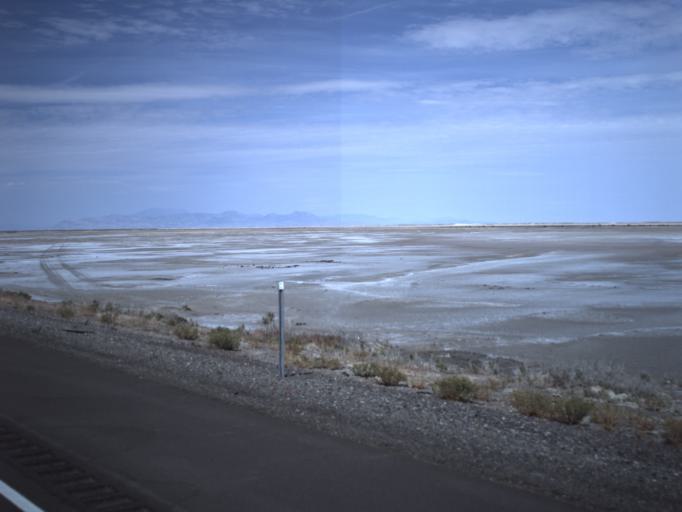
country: US
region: Utah
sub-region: Tooele County
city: Wendover
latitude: 40.7282
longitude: -113.3036
